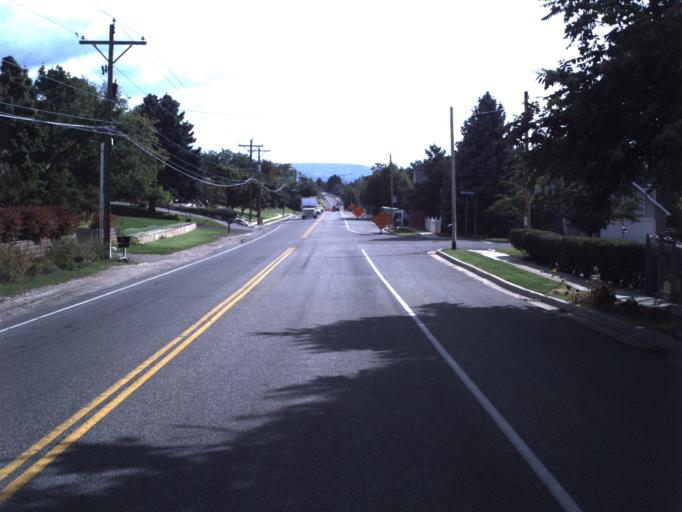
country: US
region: Utah
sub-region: Davis County
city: Farmington
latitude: 40.9589
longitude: -111.8834
